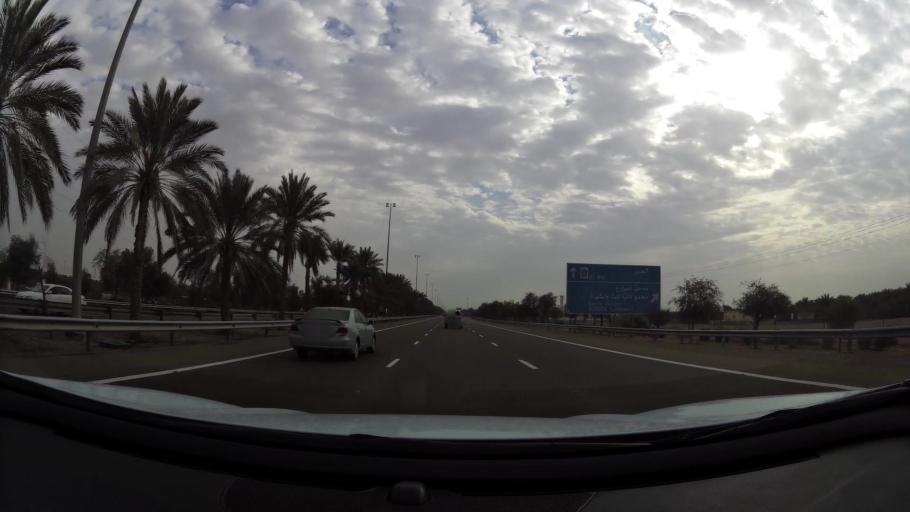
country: AE
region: Abu Dhabi
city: Al Ain
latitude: 24.2043
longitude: 55.4222
